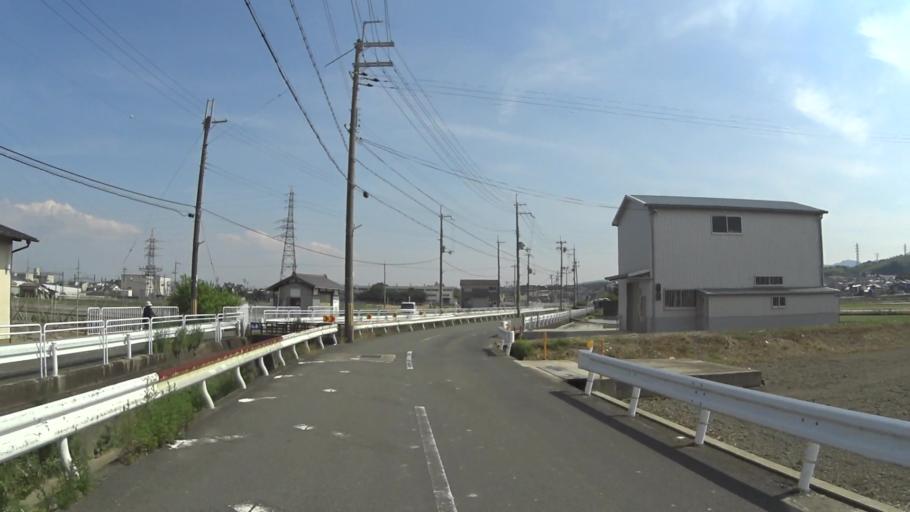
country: JP
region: Kyoto
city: Muko
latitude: 34.9633
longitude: 135.7015
